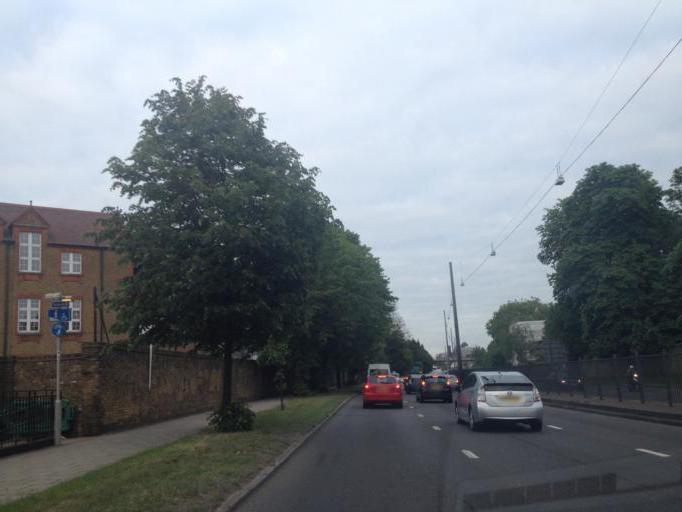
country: GB
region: England
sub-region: Greater London
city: Acton
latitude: 51.4877
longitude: -0.2582
